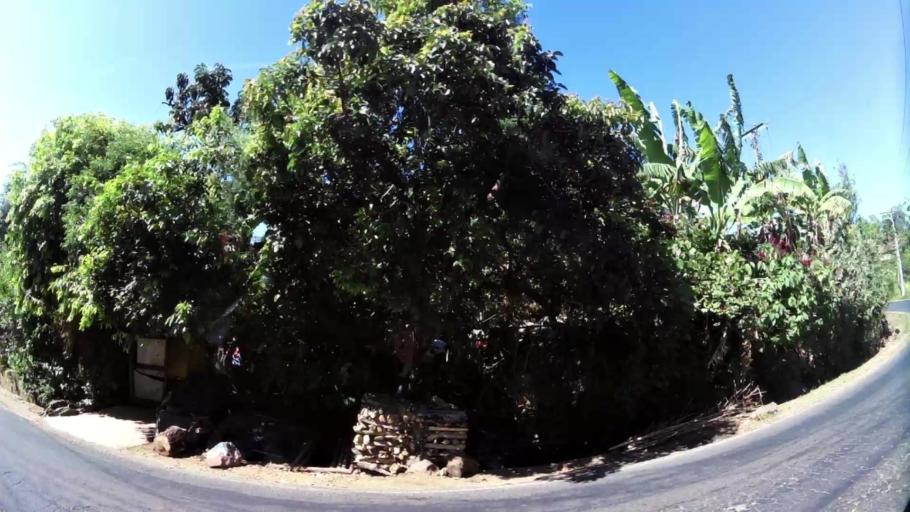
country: SV
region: Ahuachapan
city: Ahuachapan
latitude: 13.9116
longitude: -89.8326
